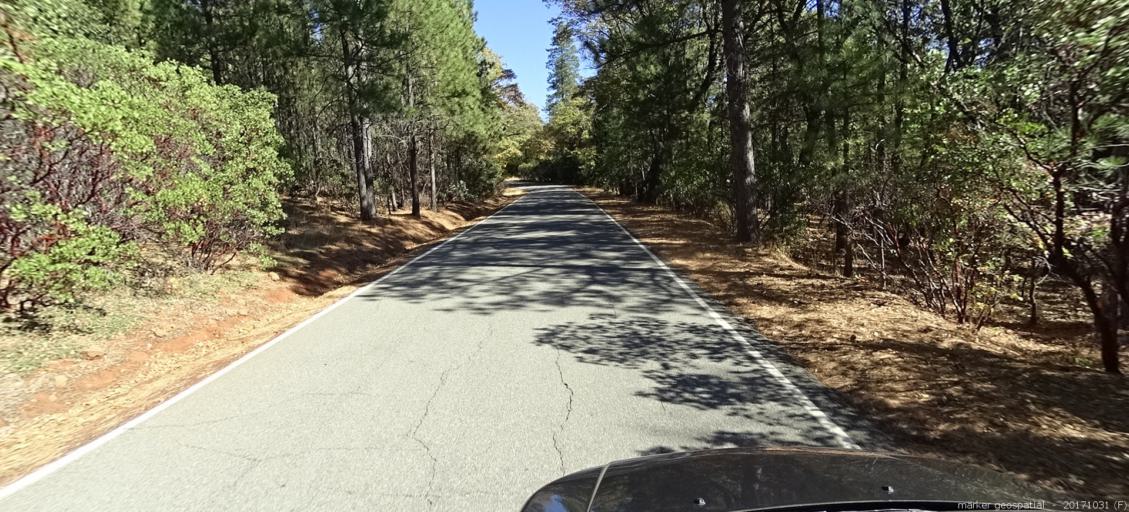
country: US
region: California
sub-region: Shasta County
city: Shingletown
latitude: 40.4729
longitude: -121.8764
